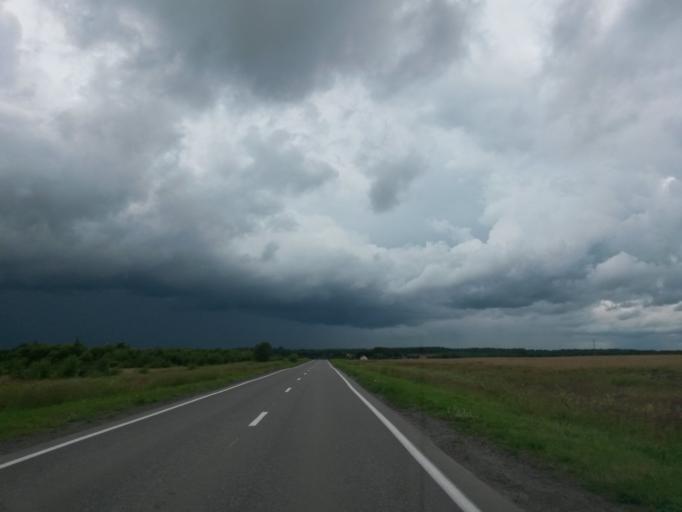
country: RU
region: Jaroslavl
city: Konstantinovskiy
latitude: 57.8711
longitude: 39.5955
